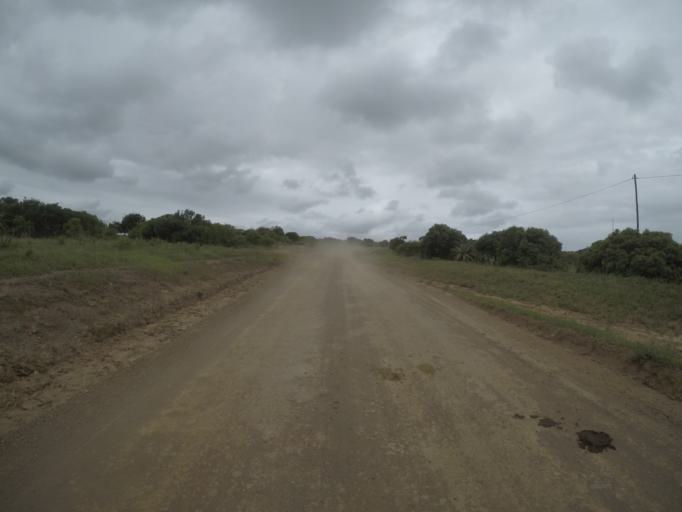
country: ZA
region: KwaZulu-Natal
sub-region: uThungulu District Municipality
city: Empangeni
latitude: -28.5991
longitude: 31.8383
